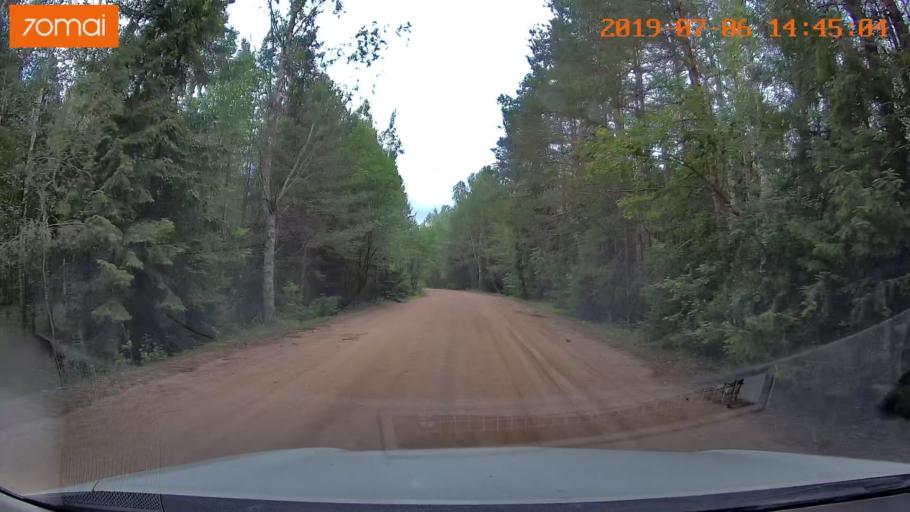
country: BY
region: Minsk
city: Ivyanyets
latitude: 53.9684
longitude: 26.6895
